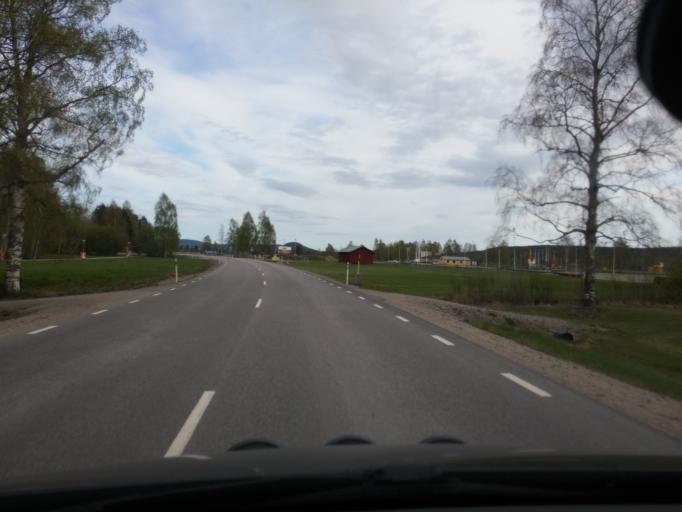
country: SE
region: Gaevleborg
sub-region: Ljusdals Kommun
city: Ljusdal
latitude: 61.8213
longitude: 16.0806
